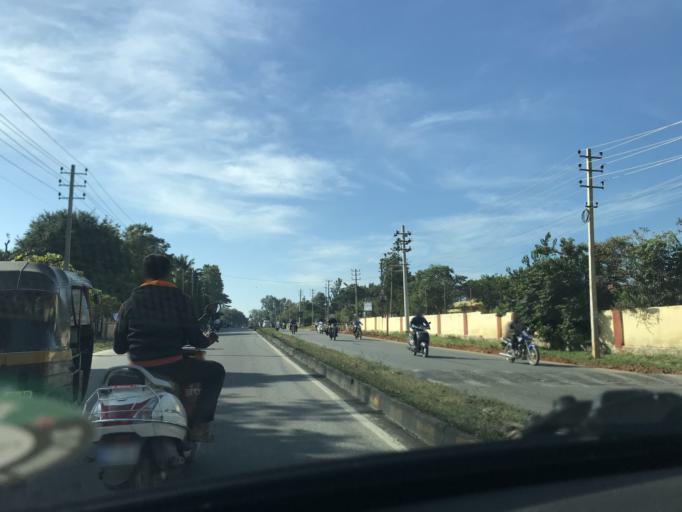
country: IN
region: Karnataka
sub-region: Mysore
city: Mysore
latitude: 12.2773
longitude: 76.6398
